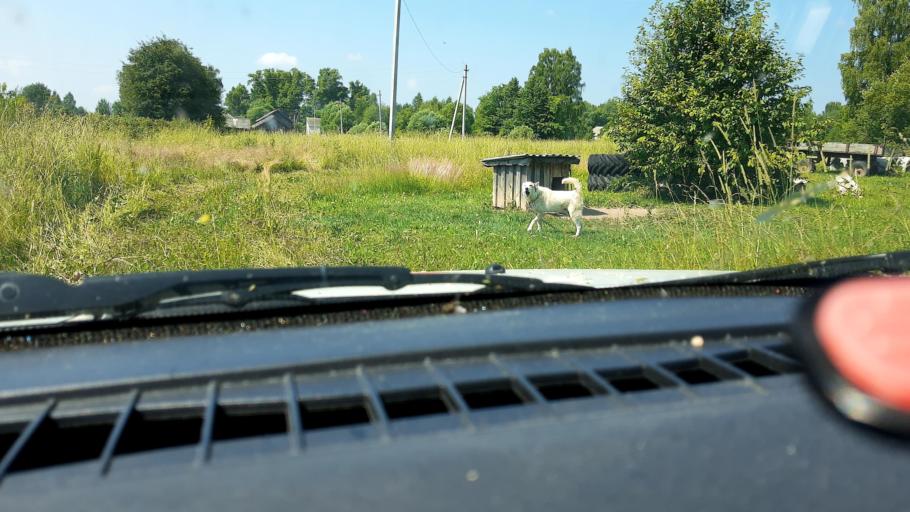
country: RU
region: Nizjnij Novgorod
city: Sharanga
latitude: 57.0414
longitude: 46.7217
